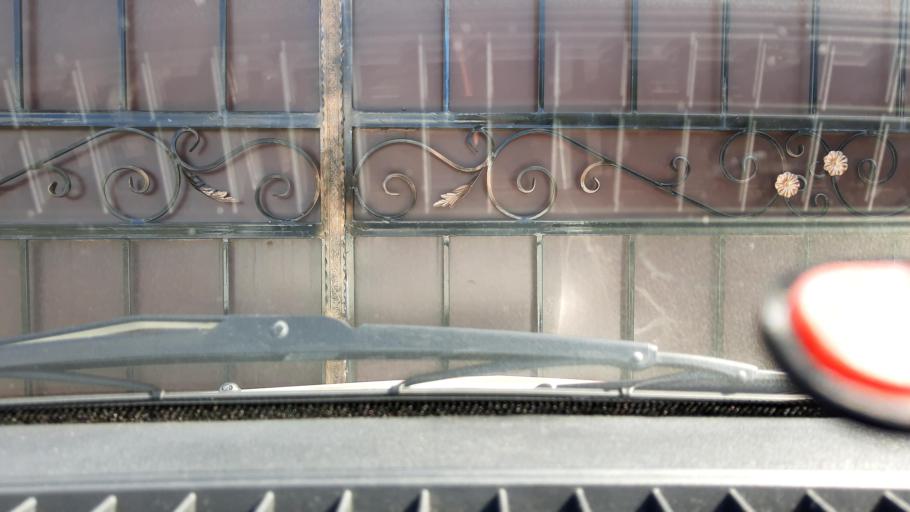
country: RU
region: Bashkortostan
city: Avdon
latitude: 54.4950
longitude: 55.8976
